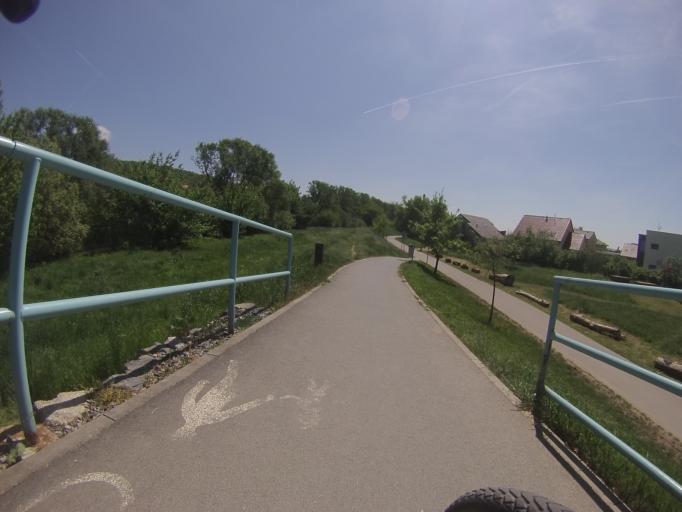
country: CZ
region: South Moravian
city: Zidlochovice
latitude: 49.0328
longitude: 16.6190
